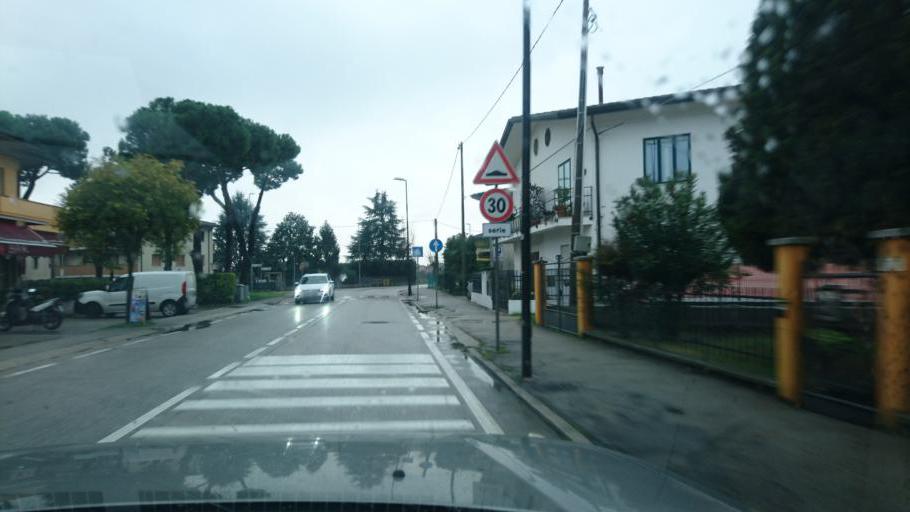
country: IT
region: Veneto
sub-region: Provincia di Padova
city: Ponte San Nicolo
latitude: 45.3699
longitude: 11.9402
